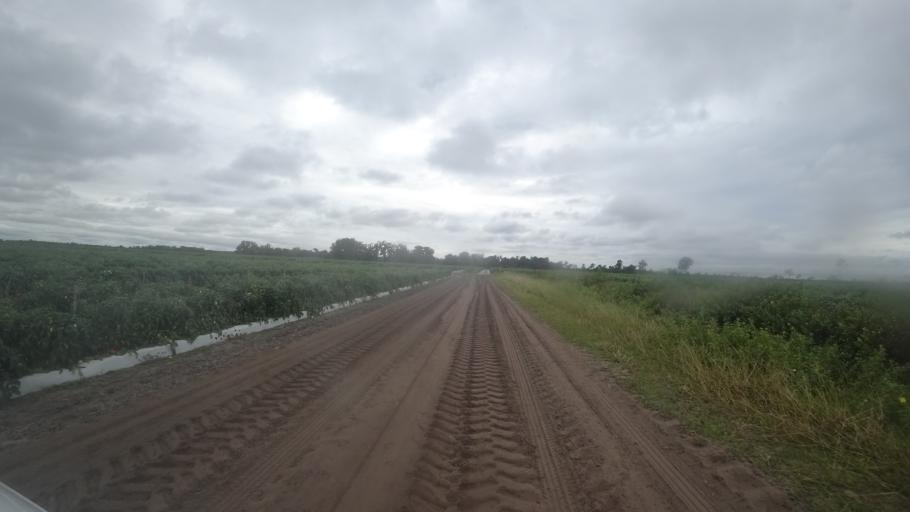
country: US
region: Florida
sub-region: Hillsborough County
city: Wimauma
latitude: 27.5644
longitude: -82.1369
